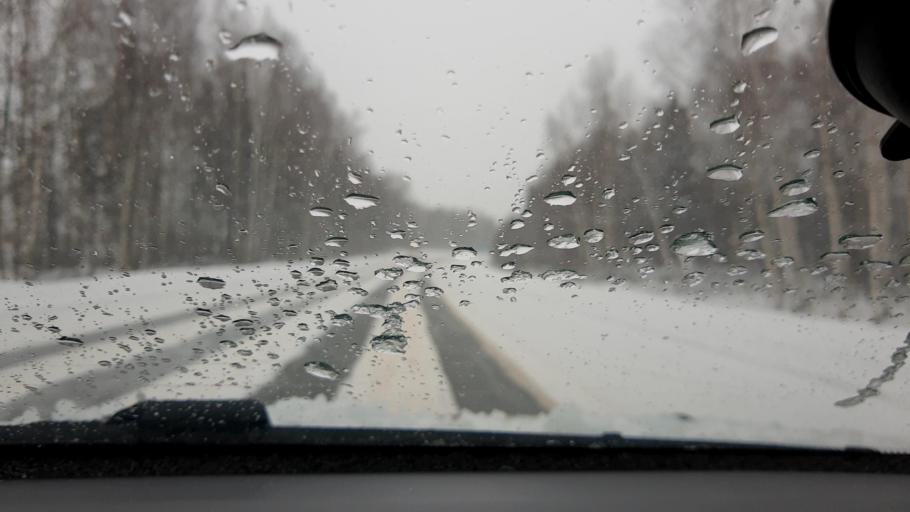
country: RU
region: Nizjnij Novgorod
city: Pervomayskiy
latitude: 56.6287
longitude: 43.2437
